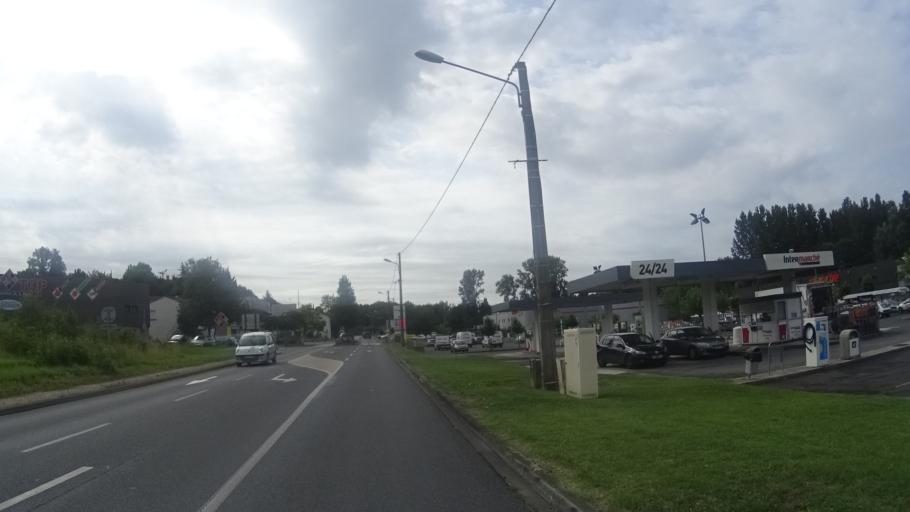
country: FR
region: Aquitaine
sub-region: Departement de la Dordogne
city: Riberac
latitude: 45.2388
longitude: 0.3472
